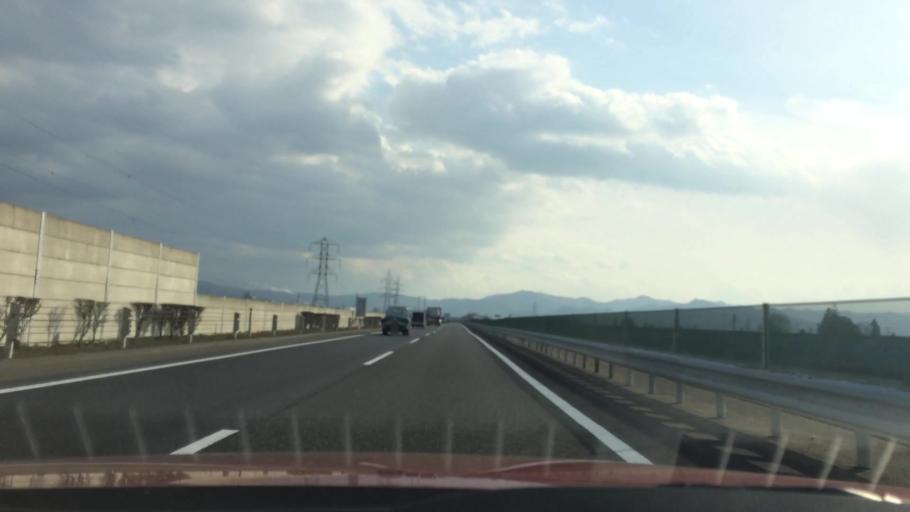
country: JP
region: Nagano
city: Matsumoto
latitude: 36.1812
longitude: 137.9400
